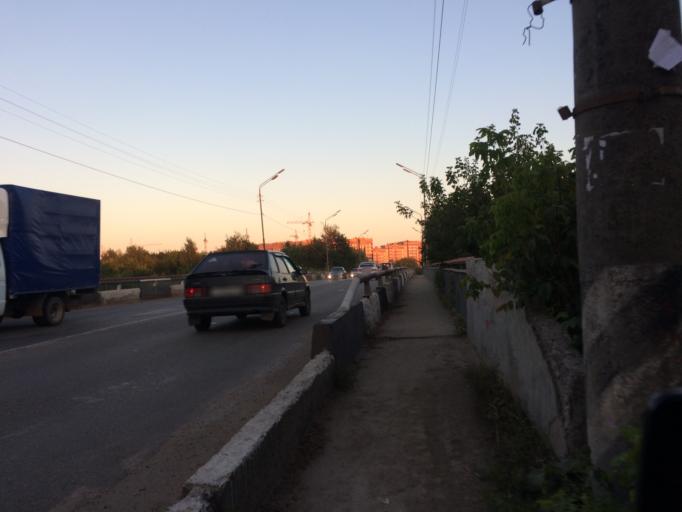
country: RU
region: Mariy-El
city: Yoshkar-Ola
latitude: 56.6448
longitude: 47.9103
